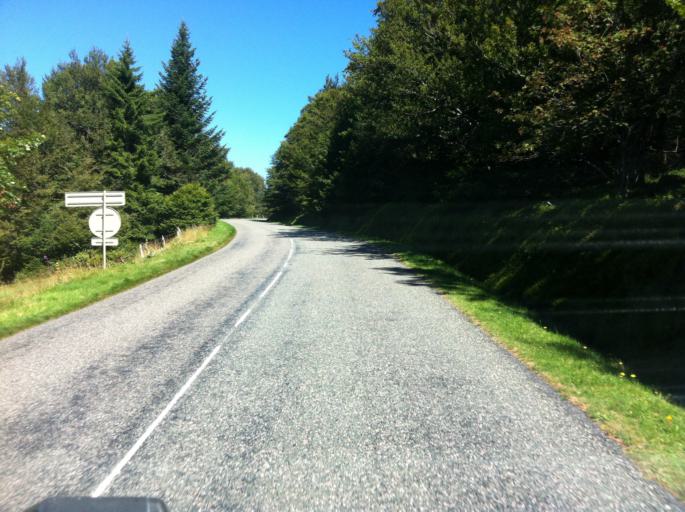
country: FR
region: Alsace
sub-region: Departement du Haut-Rhin
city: Soultzeren
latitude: 48.0977
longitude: 7.0541
